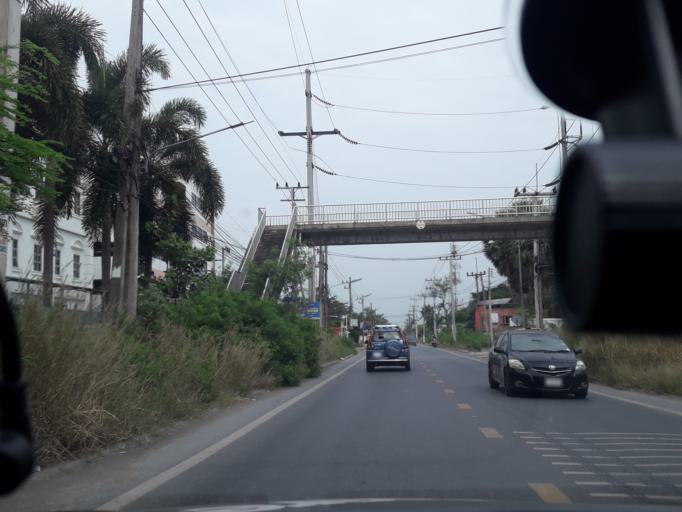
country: TH
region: Pathum Thani
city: Ban Rangsit
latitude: 14.0162
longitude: 100.7532
